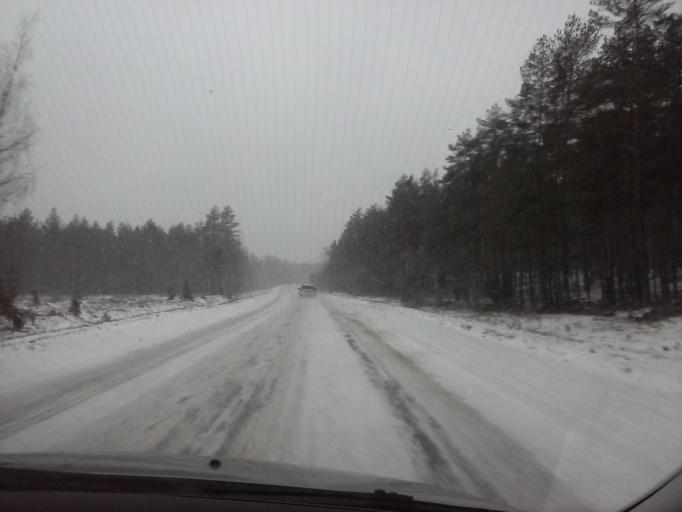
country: LV
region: Strenci
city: Seda
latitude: 57.6504
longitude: 25.8613
